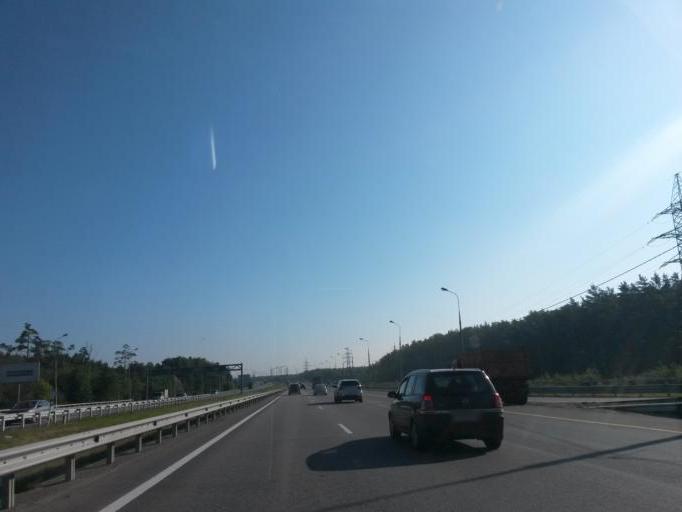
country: RU
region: Moskovskaya
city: Vostryakovo
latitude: 55.4073
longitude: 37.7875
